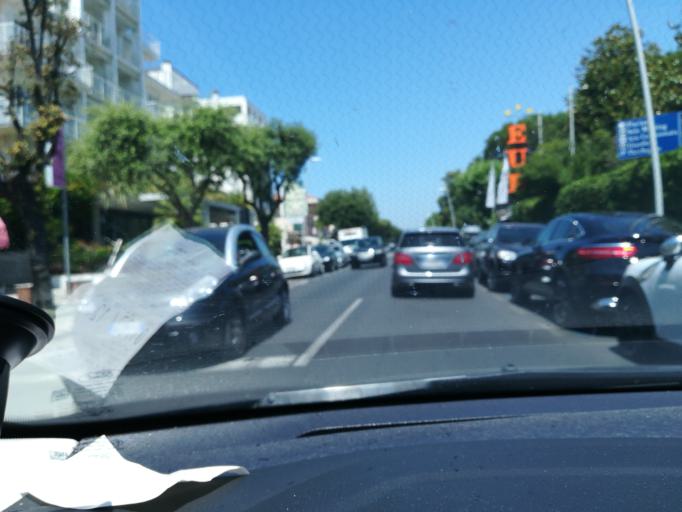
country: IT
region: Tuscany
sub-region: Provincia di Lucca
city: Camaiore
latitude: 43.8972
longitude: 10.2239
